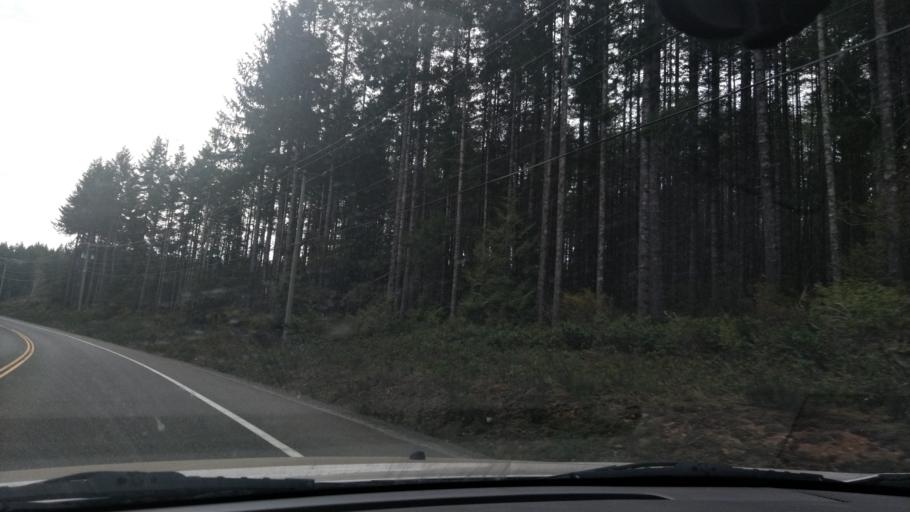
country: CA
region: British Columbia
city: Campbell River
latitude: 50.0252
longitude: -125.3532
